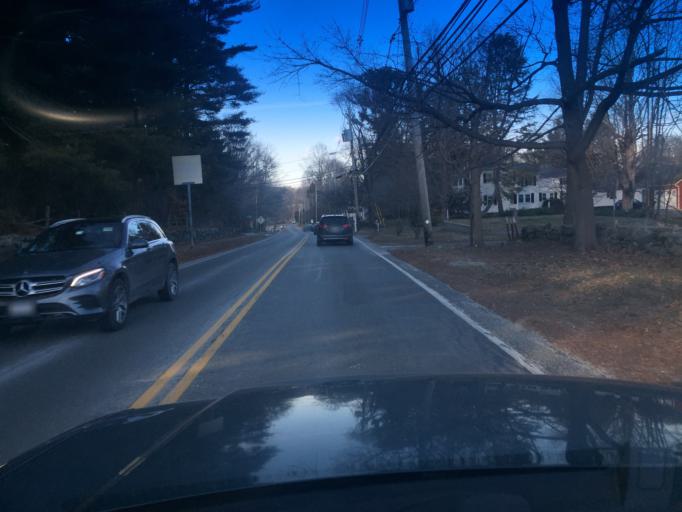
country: US
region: Massachusetts
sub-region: Middlesex County
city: Sherborn
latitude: 42.2490
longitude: -71.3688
